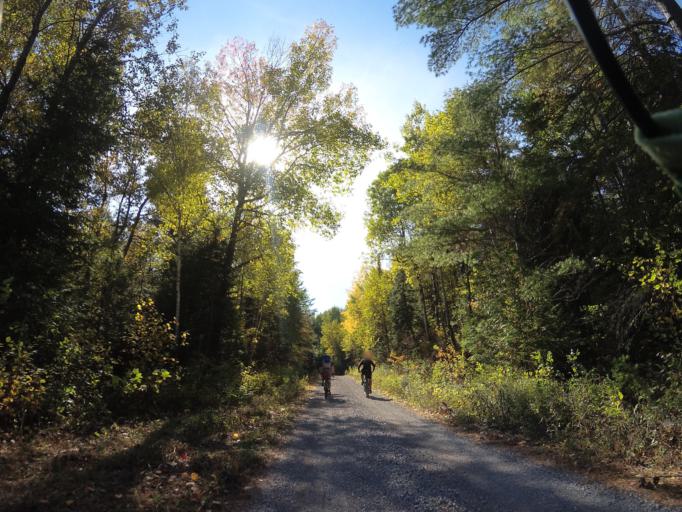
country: CA
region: Ontario
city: Pembroke
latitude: 45.3512
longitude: -77.1476
